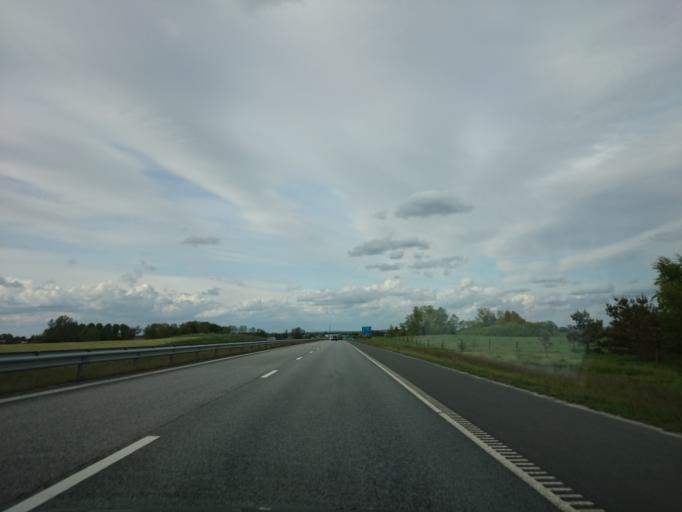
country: SE
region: Skane
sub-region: Kristianstads Kommun
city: Norra Asum
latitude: 55.9873
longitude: 14.0909
